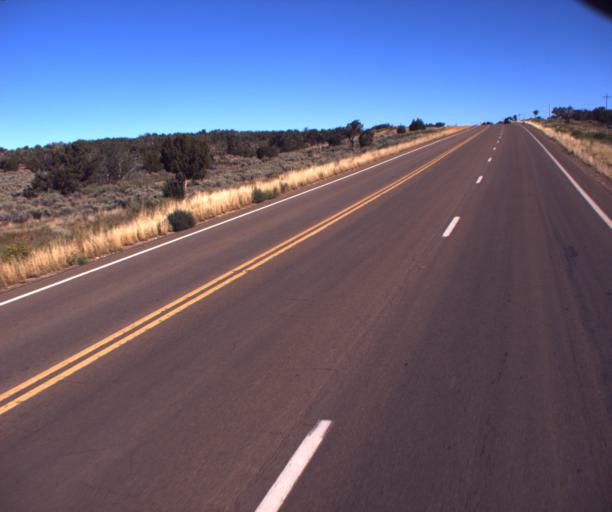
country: US
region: Arizona
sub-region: Navajo County
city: Snowflake
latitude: 34.5367
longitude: -110.0803
